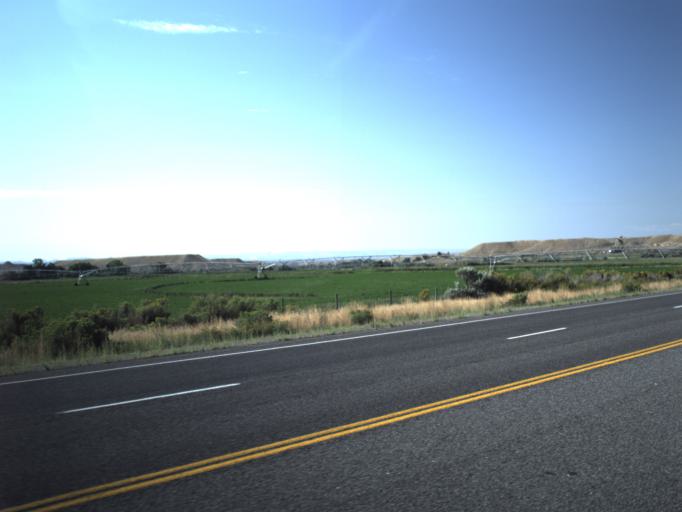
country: US
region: Utah
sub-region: Emery County
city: Huntington
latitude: 39.3548
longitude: -110.9308
